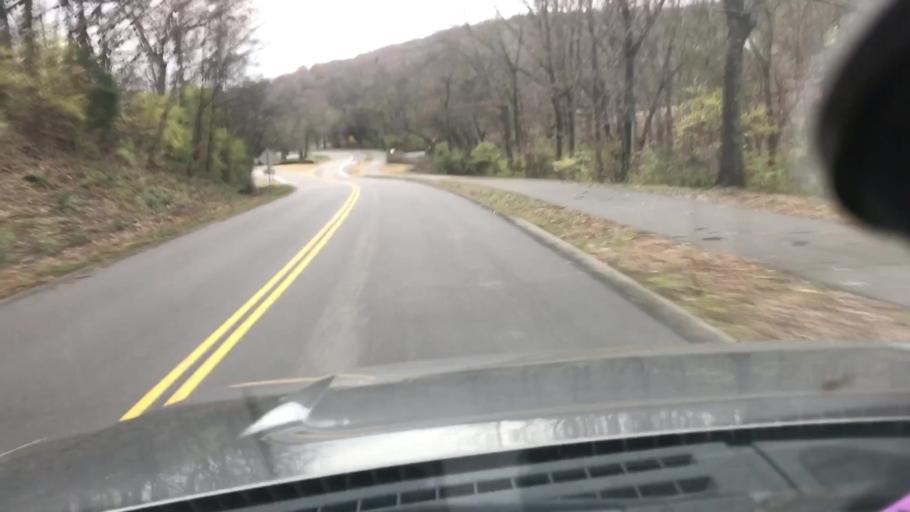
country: US
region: Tennessee
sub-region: Williamson County
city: Brentwood Estates
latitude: 35.9686
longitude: -86.7550
